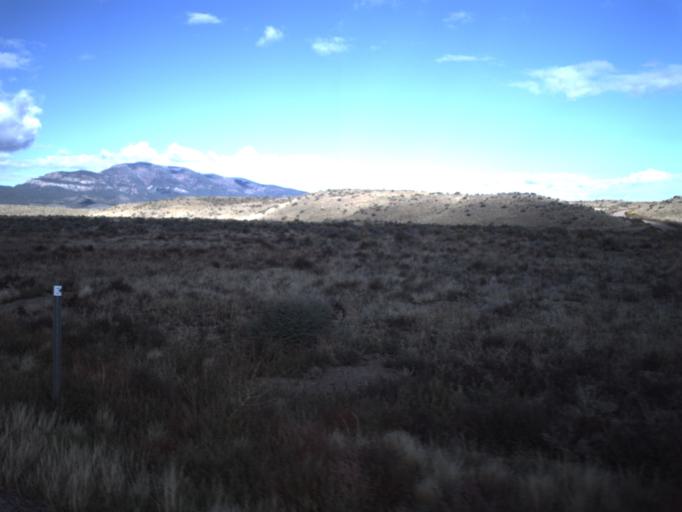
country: US
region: Utah
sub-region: Beaver County
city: Milford
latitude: 38.4392
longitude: -113.1537
